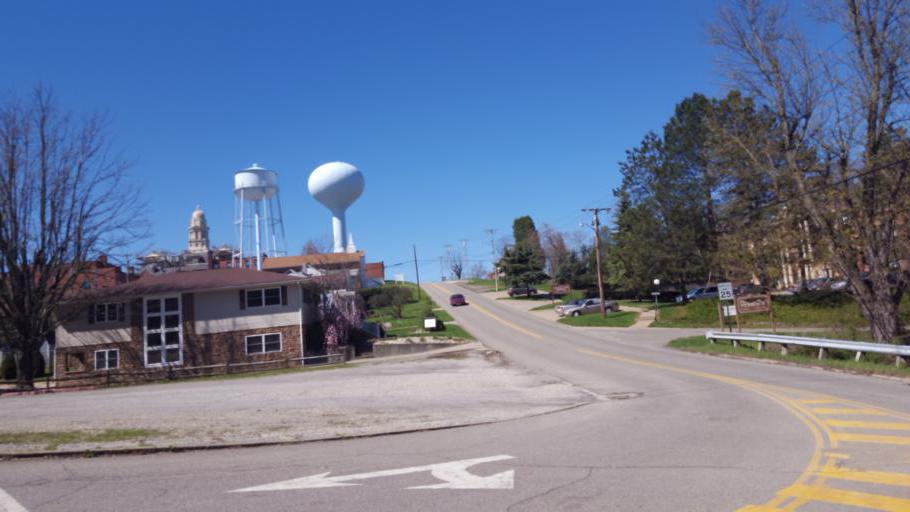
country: US
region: Ohio
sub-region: Belmont County
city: Saint Clairsville
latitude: 40.0822
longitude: -80.8980
